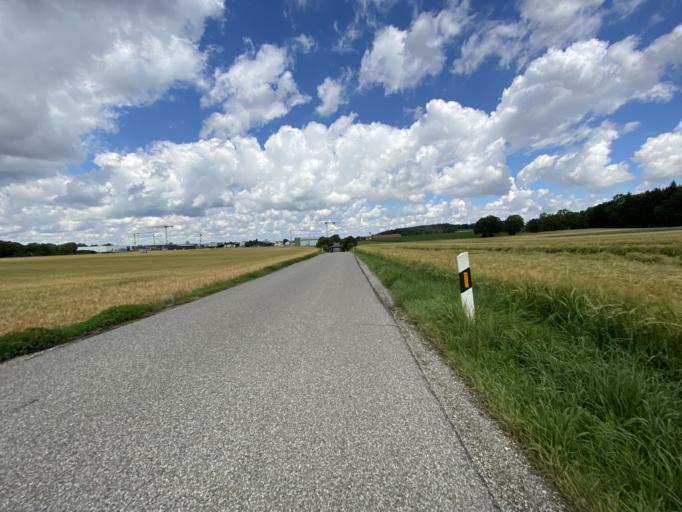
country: DE
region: Bavaria
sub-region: Upper Bavaria
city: Gilching
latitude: 48.0996
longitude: 11.3149
